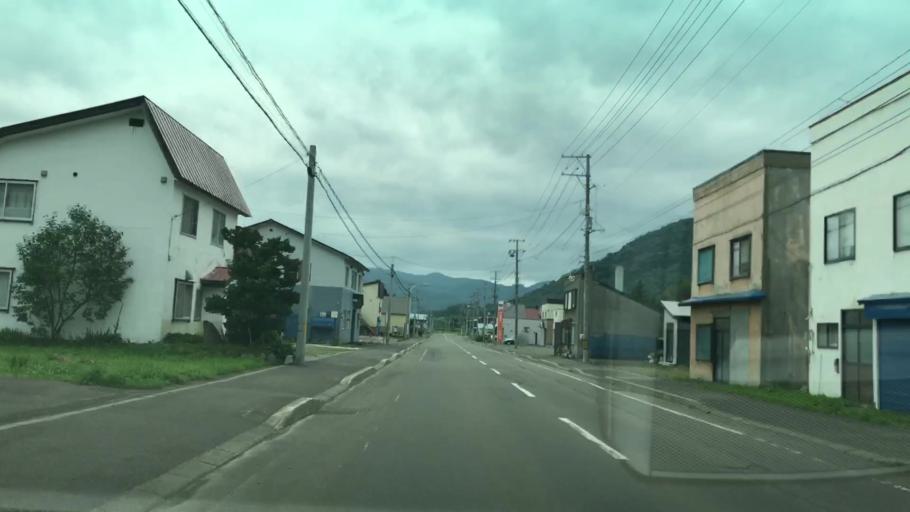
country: JP
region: Hokkaido
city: Yoichi
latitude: 43.0836
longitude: 140.8160
